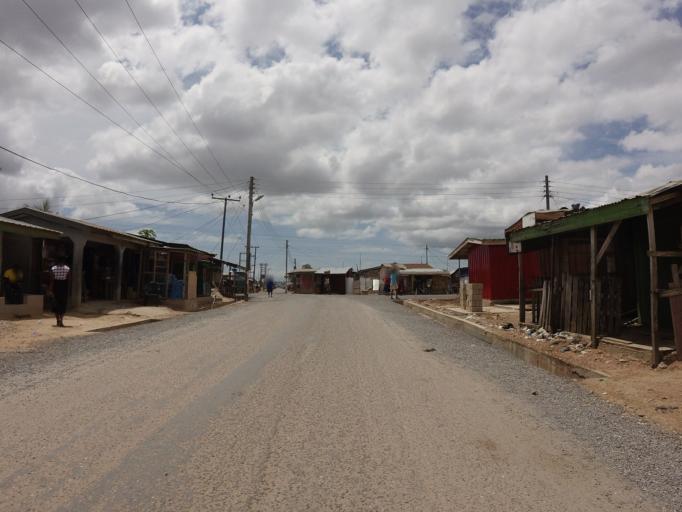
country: GH
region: Central
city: Kasoa
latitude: 5.5428
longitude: -0.3985
